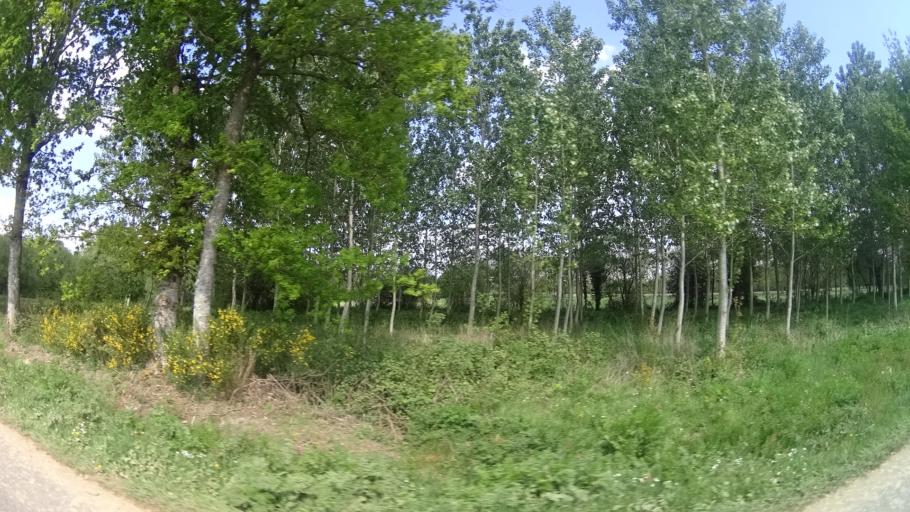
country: FR
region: Brittany
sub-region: Departement du Morbihan
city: Beganne
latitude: 47.6006
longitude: -2.1960
